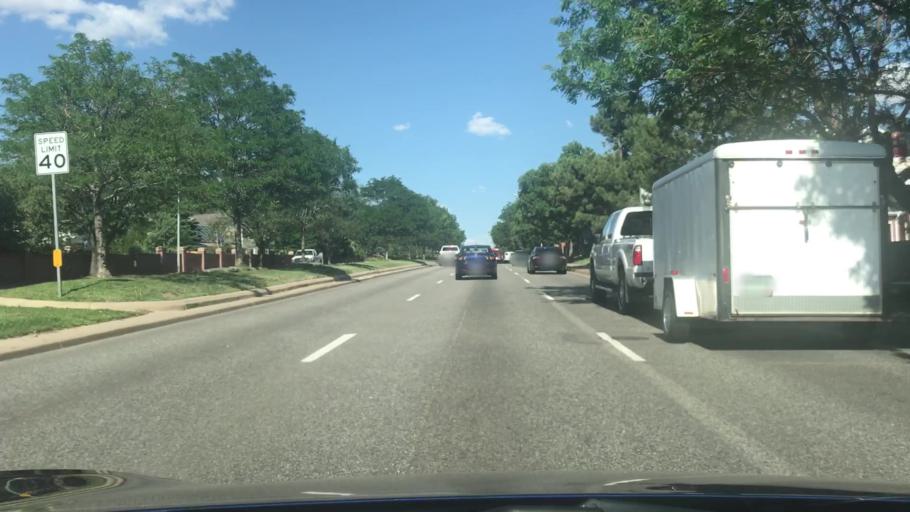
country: US
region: Colorado
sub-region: Arapahoe County
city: Dove Valley
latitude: 39.6530
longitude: -104.8272
